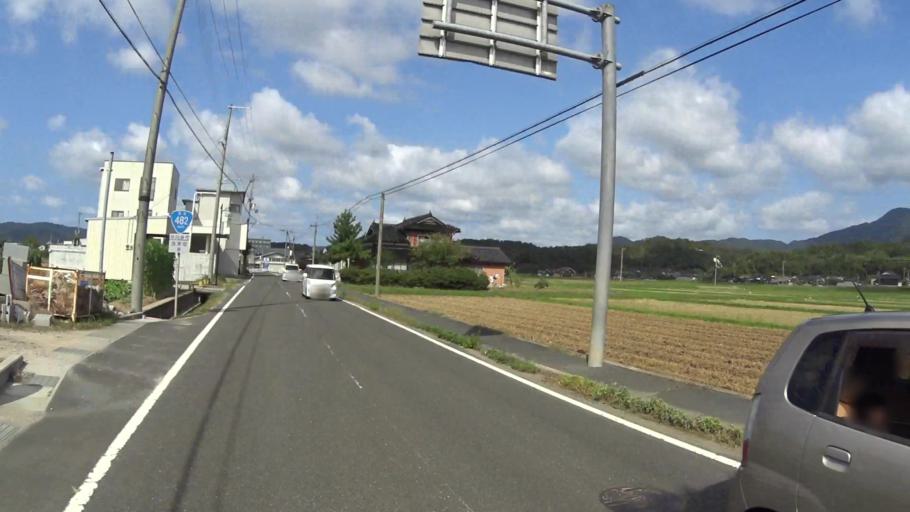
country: JP
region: Kyoto
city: Miyazu
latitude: 35.6507
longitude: 135.0920
